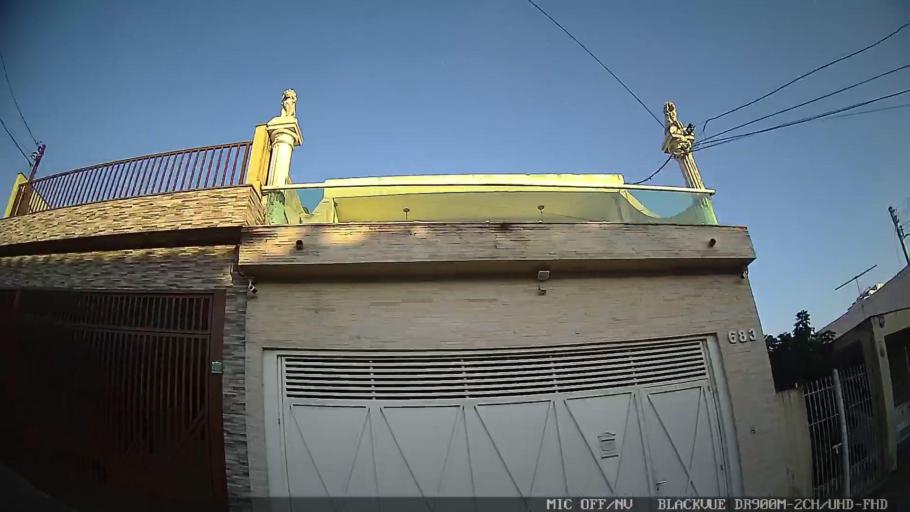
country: BR
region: Sao Paulo
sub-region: Sao Caetano Do Sul
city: Sao Caetano do Sul
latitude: -23.5815
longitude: -46.5503
